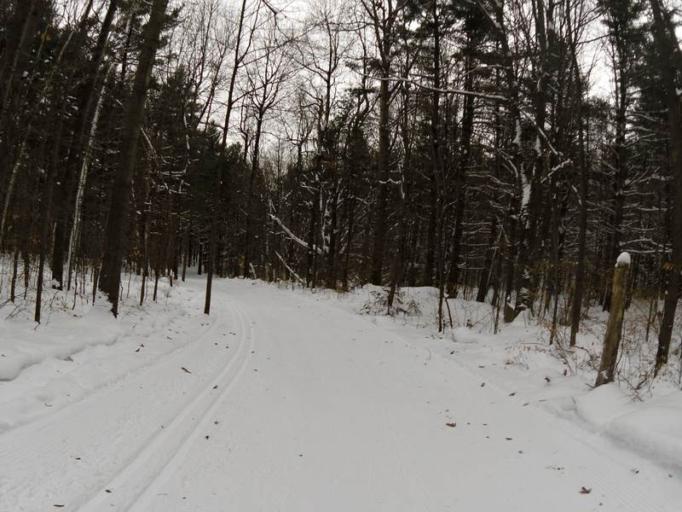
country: CA
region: Quebec
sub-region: Outaouais
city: Gatineau
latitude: 45.4937
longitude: -75.8434
